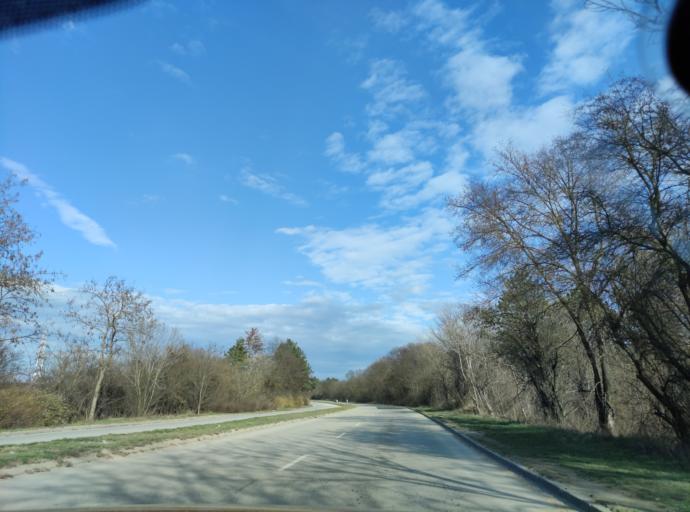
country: BG
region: Pleven
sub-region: Obshtina Dolna Mitropoliya
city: Dolna Mitropoliya
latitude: 43.4338
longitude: 24.5547
